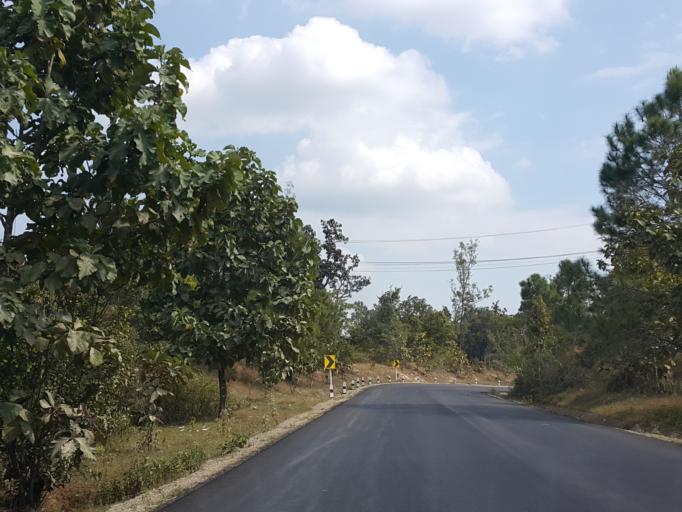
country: TH
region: Chiang Mai
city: Om Koi
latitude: 17.8201
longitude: 98.3645
